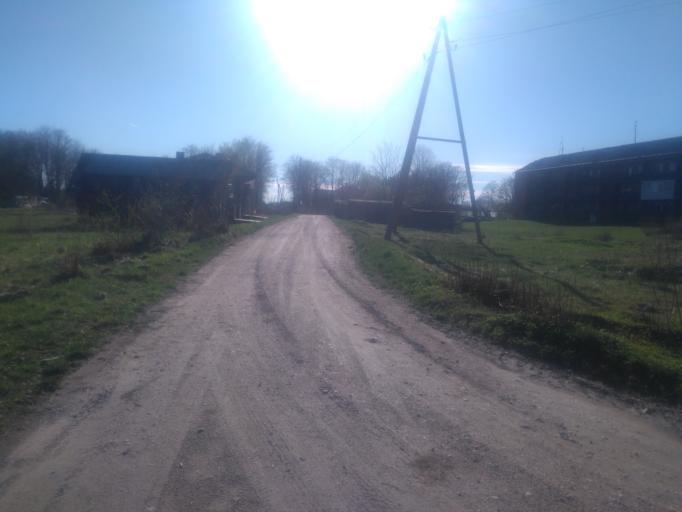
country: LV
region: Vecpiebalga
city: Vecpiebalga
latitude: 57.0169
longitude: 25.8344
